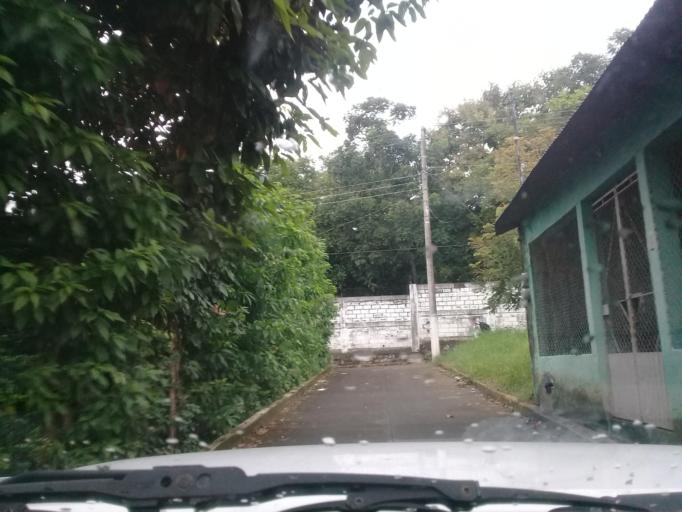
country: MX
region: Veracruz
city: San Andres Tuxtla
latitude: 18.4407
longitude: -95.2077
